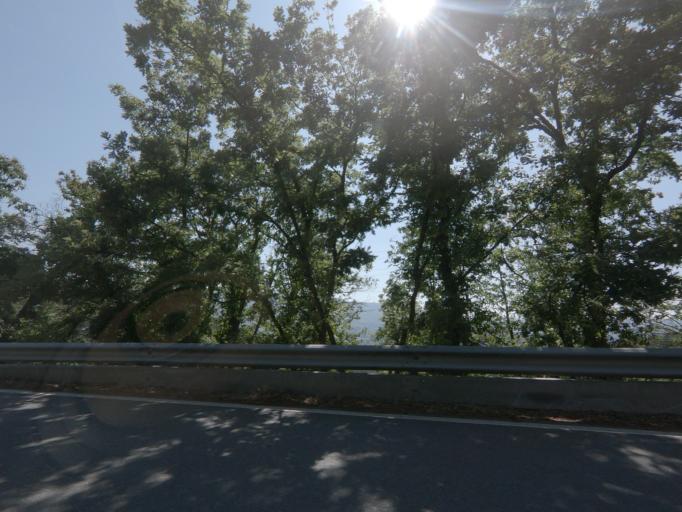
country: PT
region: Viseu
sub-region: Tarouca
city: Tarouca
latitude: 41.0375
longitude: -7.7410
